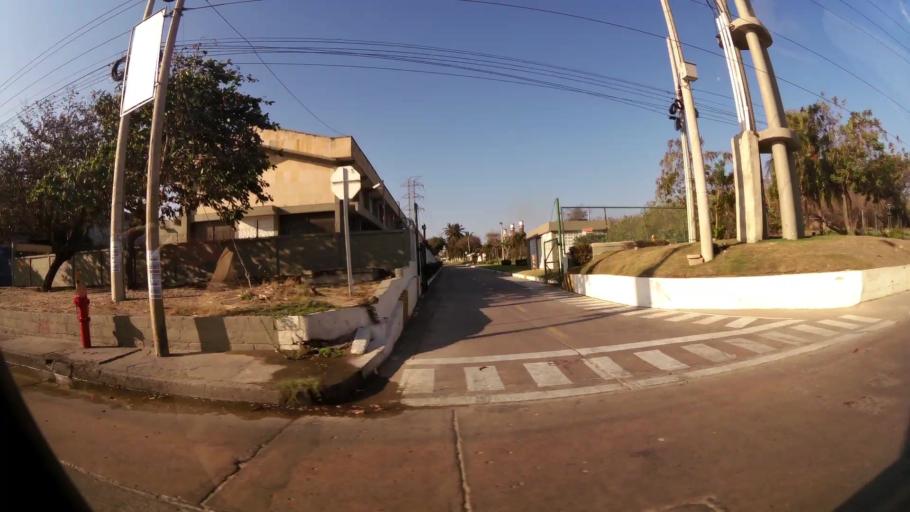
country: CO
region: Atlantico
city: Barranquilla
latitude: 11.0299
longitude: -74.8071
